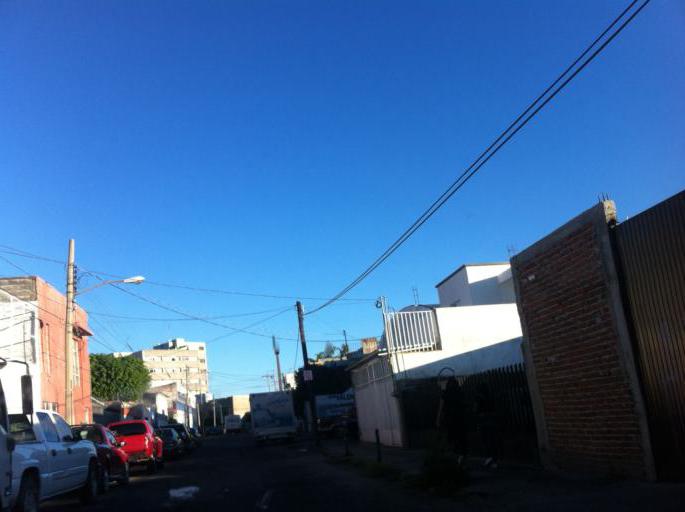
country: MX
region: Guanajuato
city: Leon
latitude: 21.1106
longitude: -101.6907
